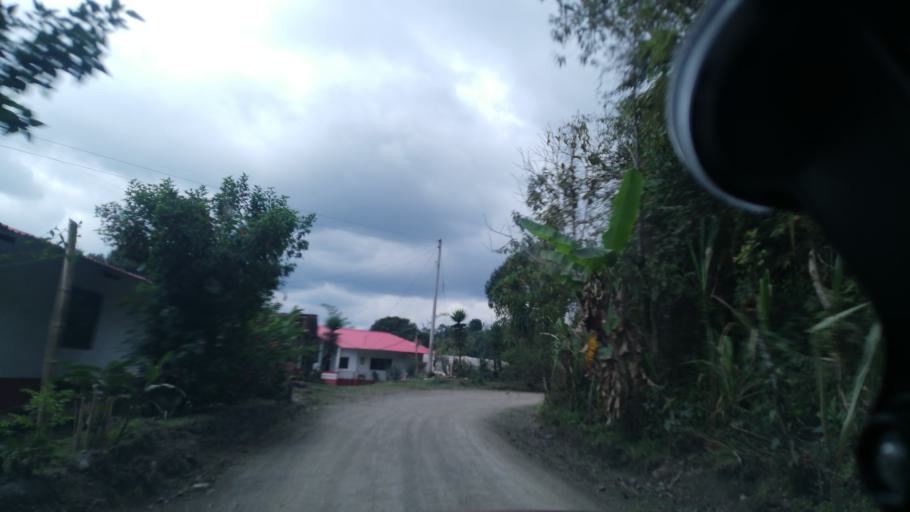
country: CO
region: Cundinamarca
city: Pacho
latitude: 5.1561
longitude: -74.2482
